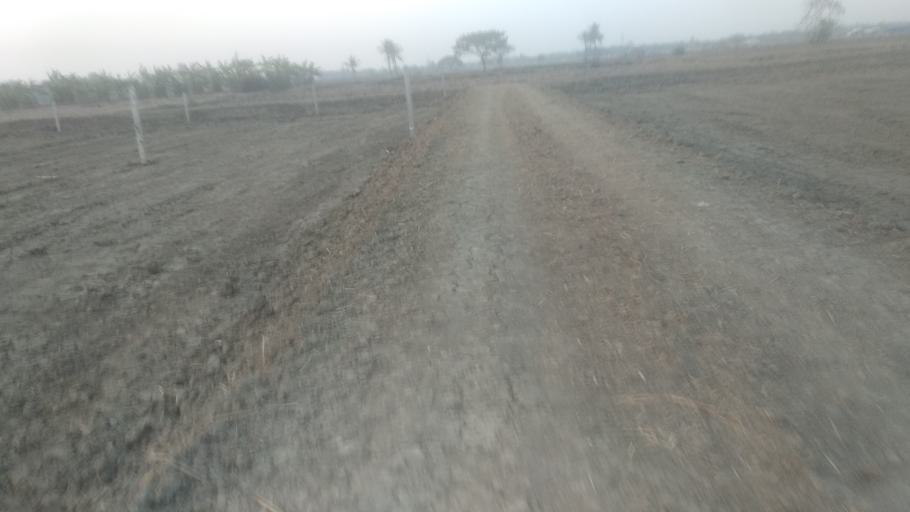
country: MM
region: Yangon
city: Kanbe
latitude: 16.8811
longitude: 95.9779
